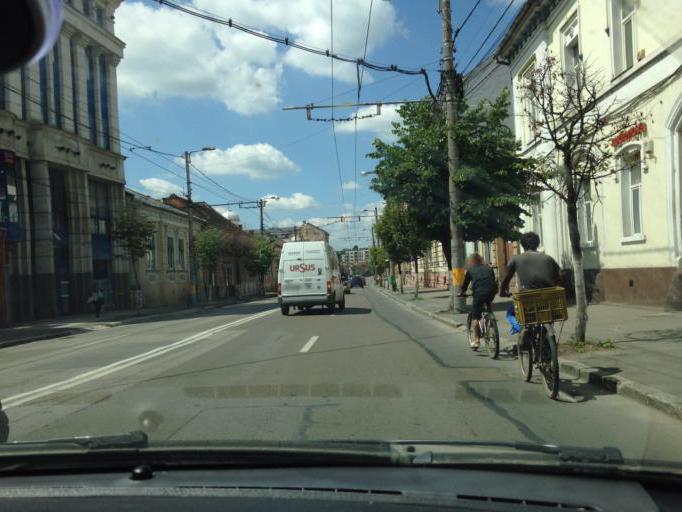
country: RO
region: Cluj
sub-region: Municipiul Cluj-Napoca
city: Cluj-Napoca
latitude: 46.7683
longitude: 23.5841
